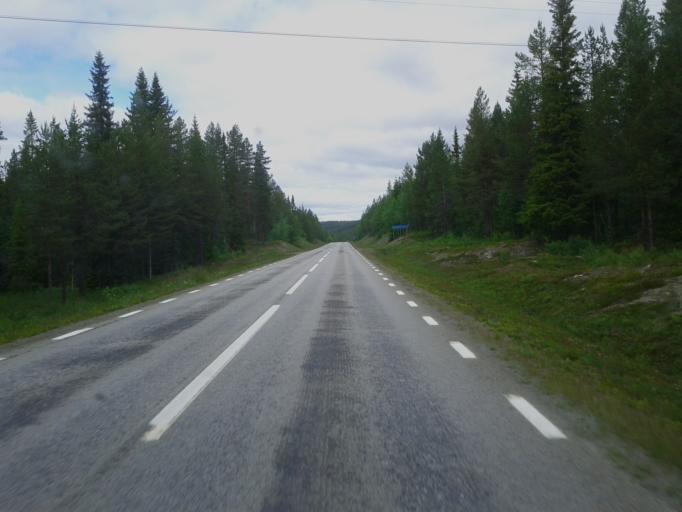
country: SE
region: Vaesterbotten
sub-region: Storumans Kommun
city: Fristad
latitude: 65.3696
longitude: 16.5188
